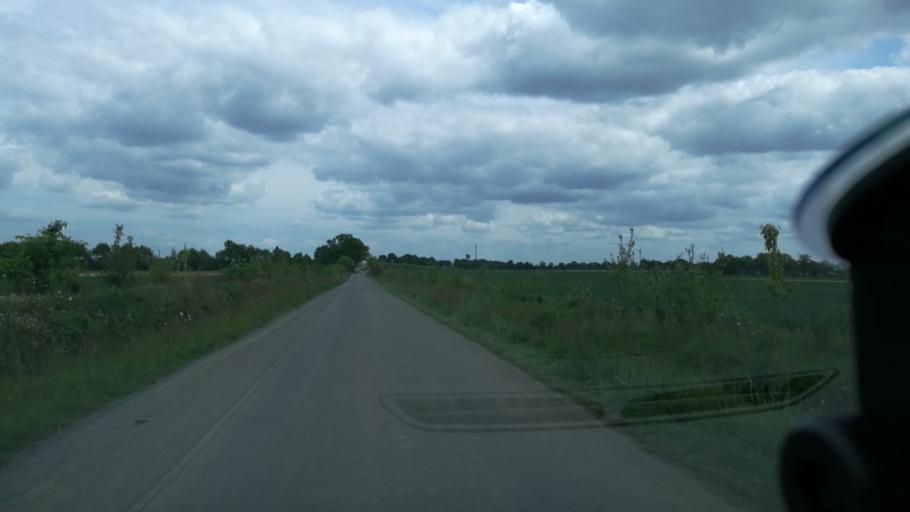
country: FR
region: Brittany
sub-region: Departement d'Ille-et-Vilaine
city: Retiers
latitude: 47.8927
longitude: -1.3783
